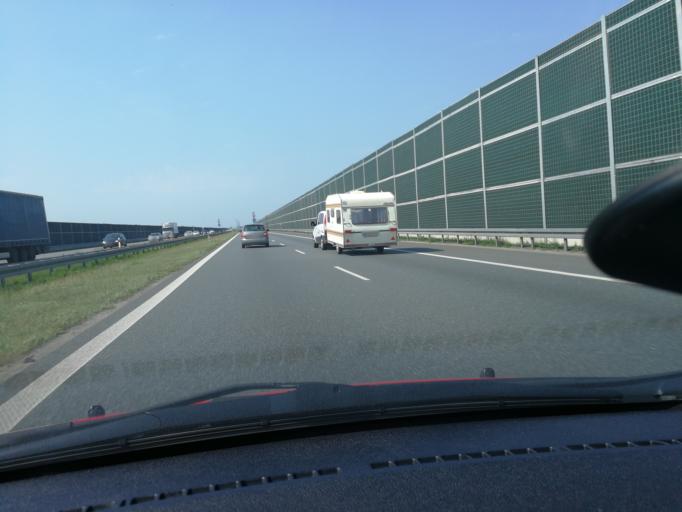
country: PL
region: Masovian Voivodeship
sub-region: Powiat zyrardowski
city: Zyrardow
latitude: 52.1142
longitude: 20.4836
